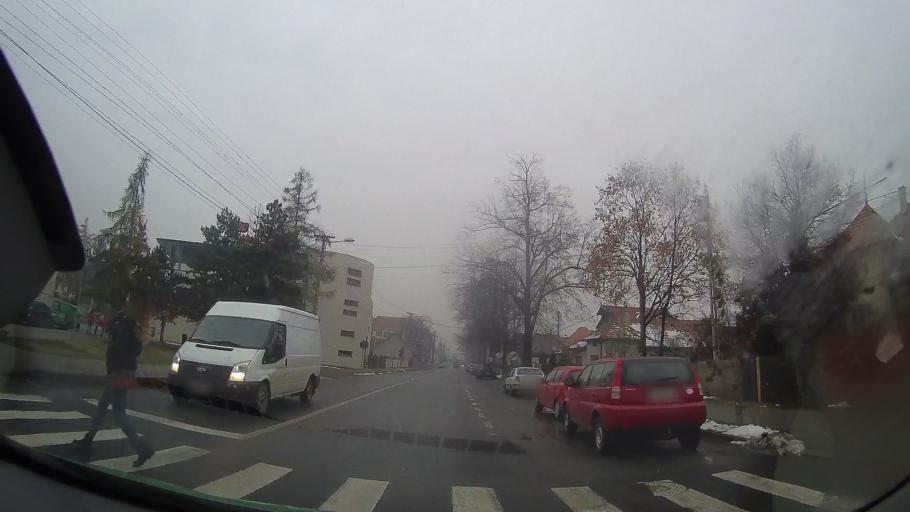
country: RO
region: Harghita
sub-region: Municipiul Gheorgheni
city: Gheorgheni
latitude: 46.7232
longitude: 25.5980
